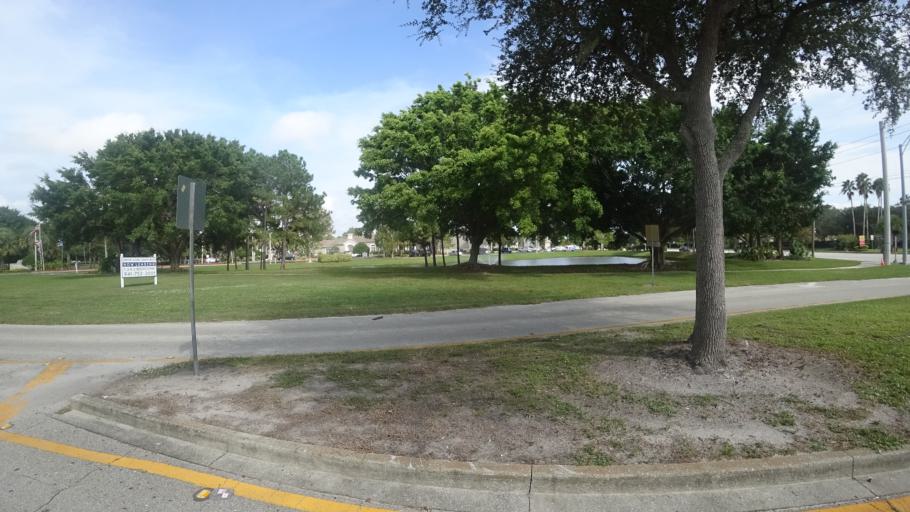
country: US
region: Florida
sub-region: Manatee County
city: Bayshore Gardens
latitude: 27.4483
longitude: -82.6074
